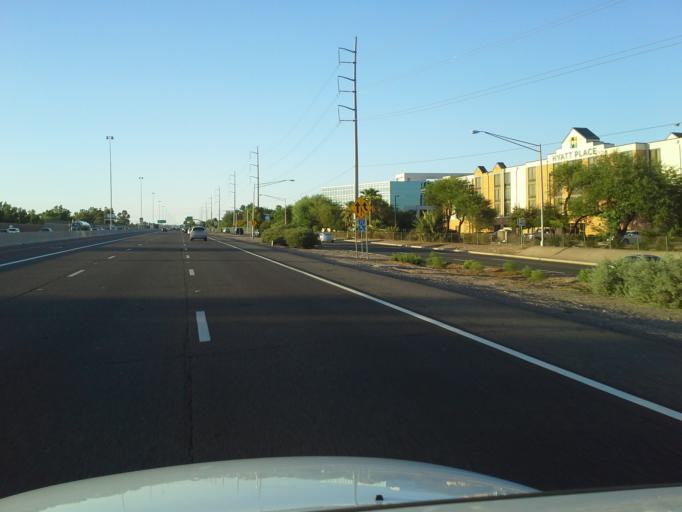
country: US
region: Arizona
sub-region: Maricopa County
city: Glendale
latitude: 33.5842
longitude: -112.1168
